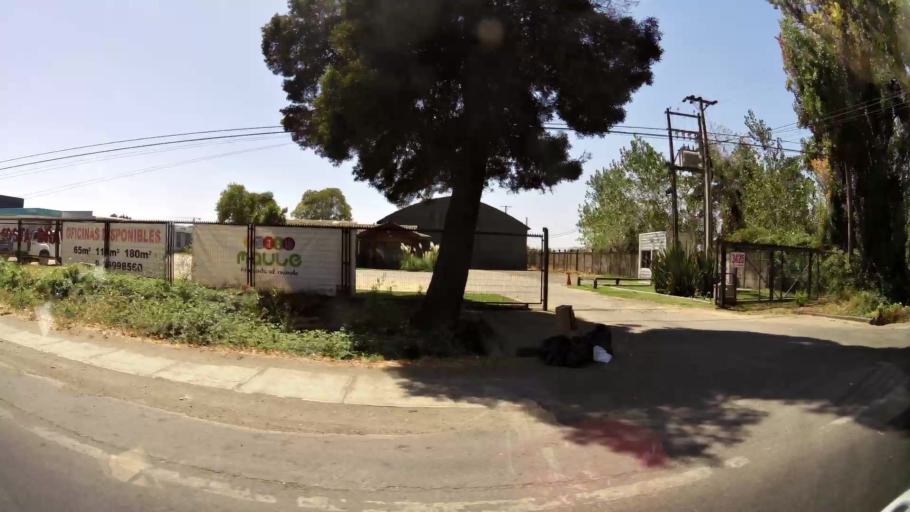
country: CL
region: Maule
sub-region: Provincia de Talca
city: Talca
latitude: -35.4355
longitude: -71.6258
